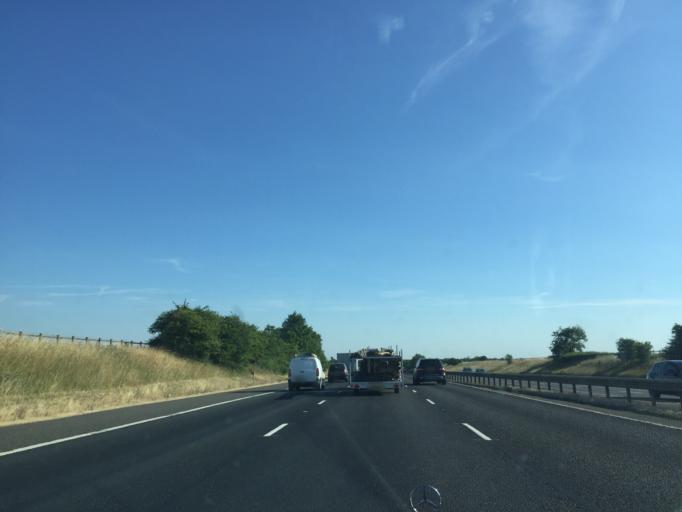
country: GB
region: England
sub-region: Oxfordshire
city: Bicester
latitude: 51.9130
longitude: -1.2043
